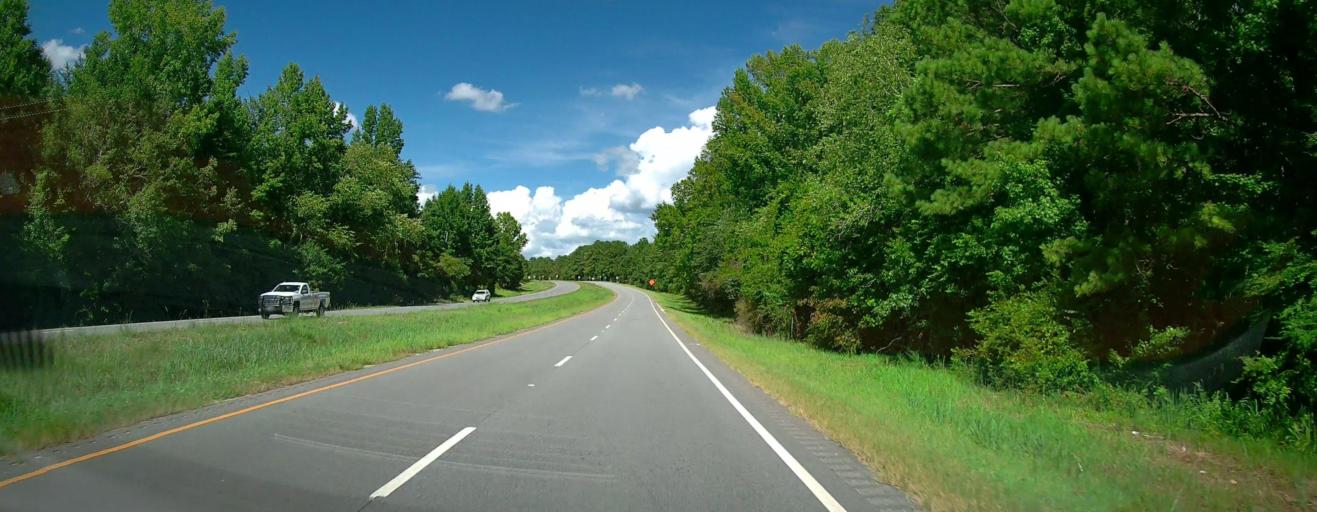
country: US
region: Alabama
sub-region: Macon County
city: Tuskegee
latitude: 32.3844
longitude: -85.7633
